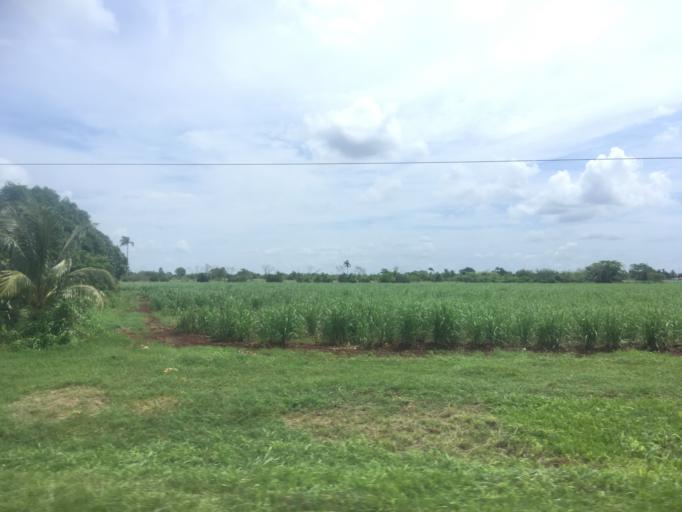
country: CU
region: Matanzas
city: Perico
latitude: 22.7813
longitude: -81.0404
